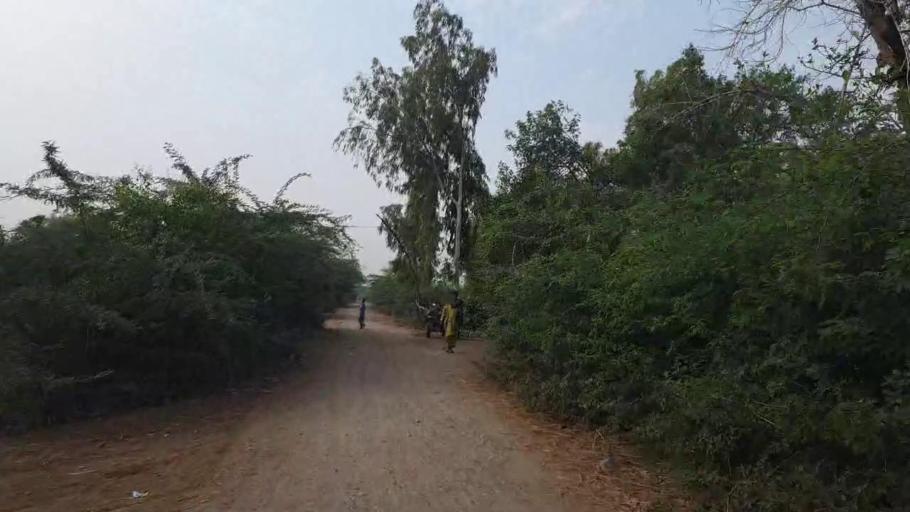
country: PK
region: Sindh
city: Tando Bago
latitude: 24.7760
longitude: 68.8717
